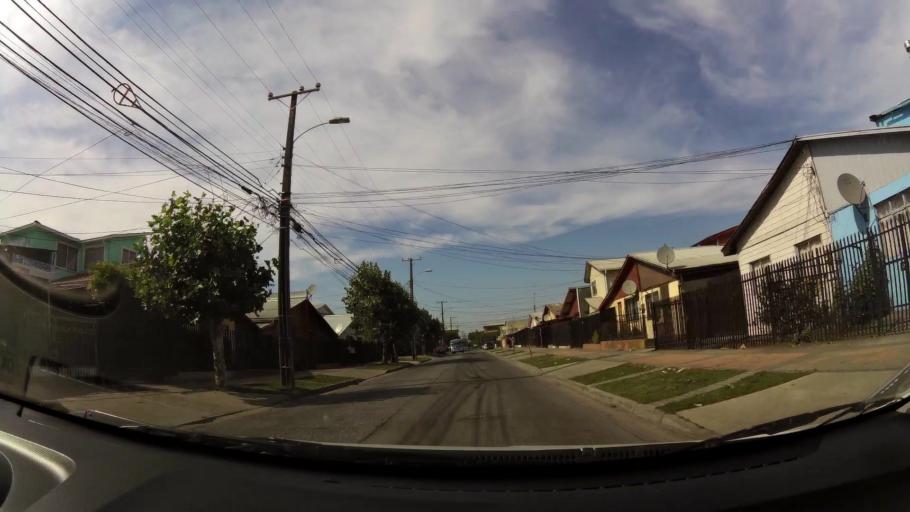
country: CL
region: Biobio
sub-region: Provincia de Concepcion
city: Talcahuano
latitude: -36.7851
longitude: -73.1040
